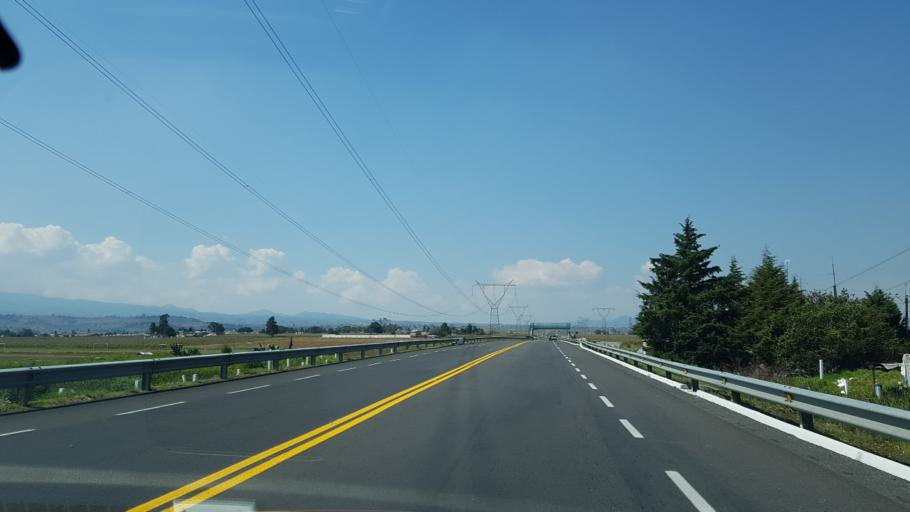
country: MX
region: Mexico
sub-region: Almoloya de Juarez
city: Fraccionamiento Colinas del Sol
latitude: 19.3865
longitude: -99.7462
